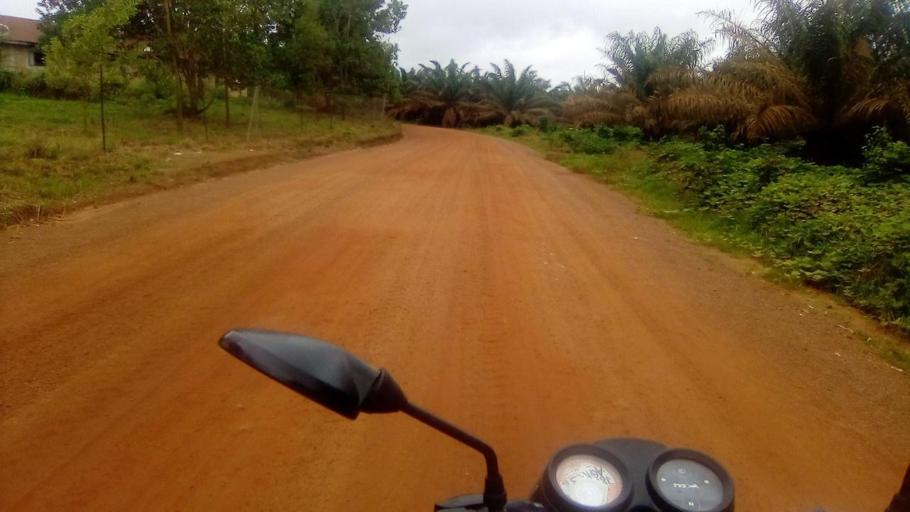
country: SL
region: Southern Province
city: Tongole
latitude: 7.4337
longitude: -11.8585
